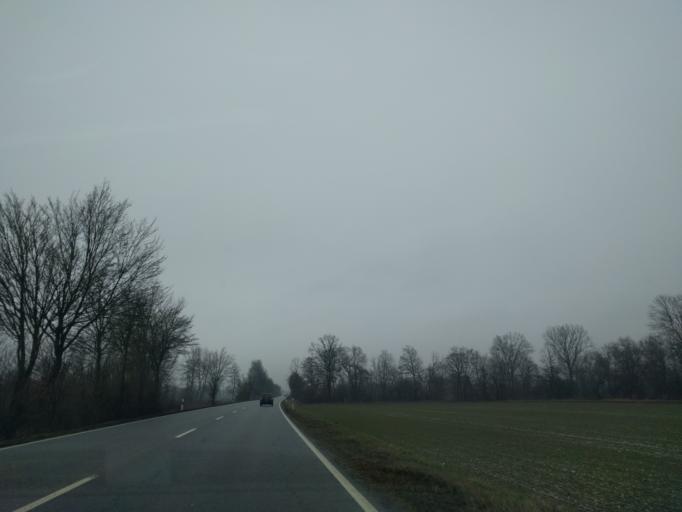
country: DE
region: Bavaria
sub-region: Lower Bavaria
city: Winzer
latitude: 48.7155
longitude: 13.0485
